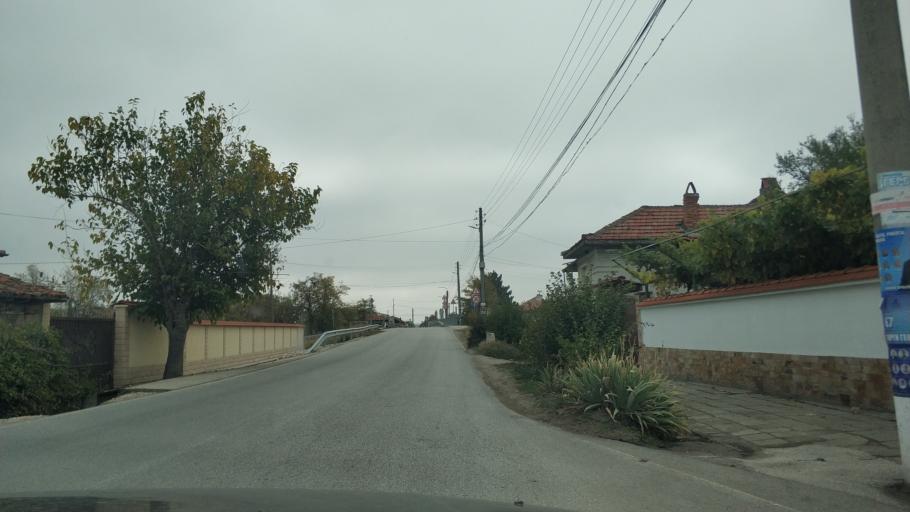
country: BG
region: Plovdiv
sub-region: Obshtina Kaloyanovo
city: Kaloyanovo
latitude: 42.3698
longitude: 24.7231
